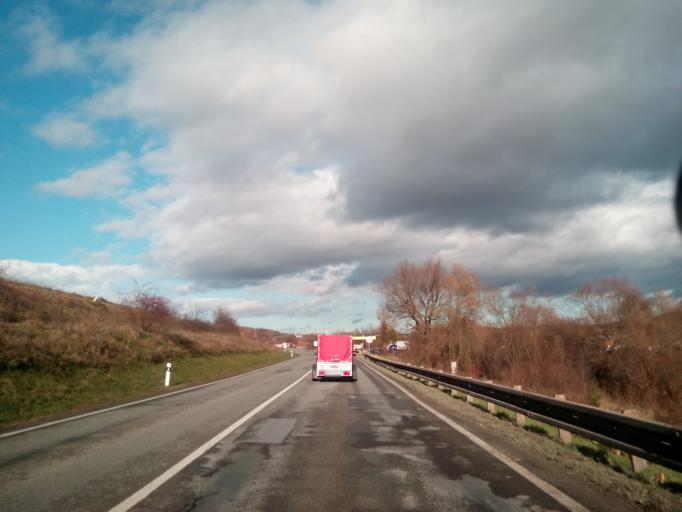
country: SK
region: Presovsky
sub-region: Okres Bardejov
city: Bardejov
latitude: 49.1416
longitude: 21.3238
